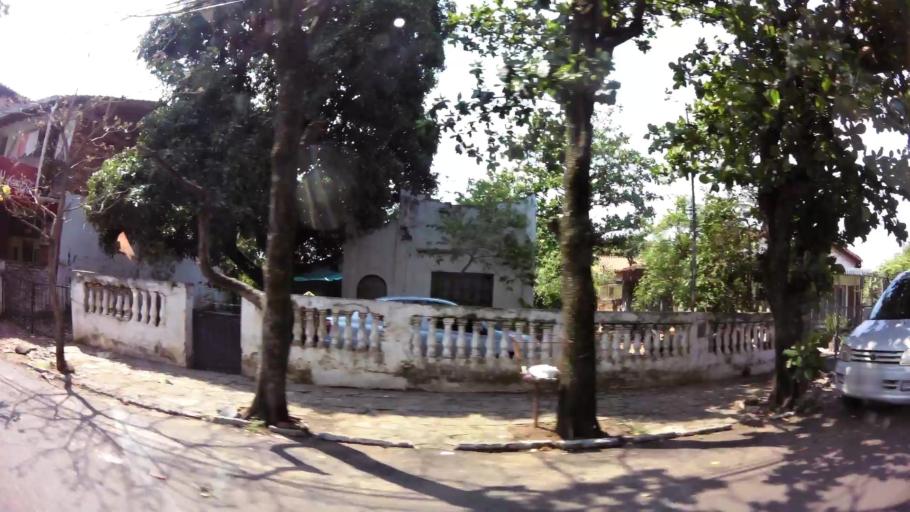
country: PY
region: Asuncion
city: Asuncion
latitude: -25.2915
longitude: -57.6532
